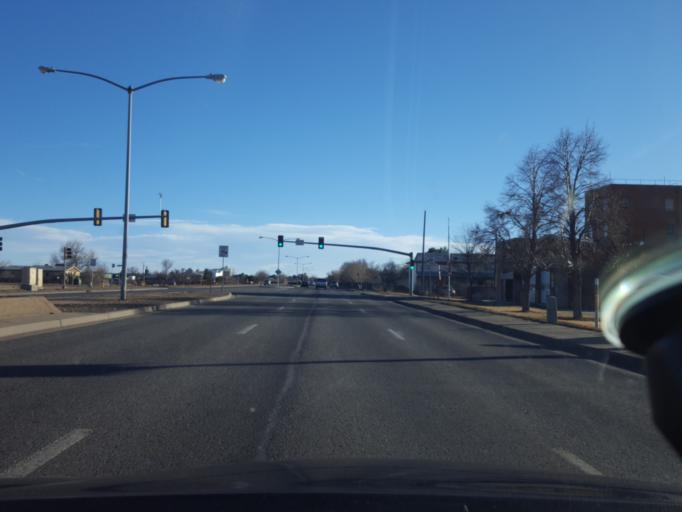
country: US
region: Colorado
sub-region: Adams County
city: Aurora
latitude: 39.7377
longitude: -104.7913
